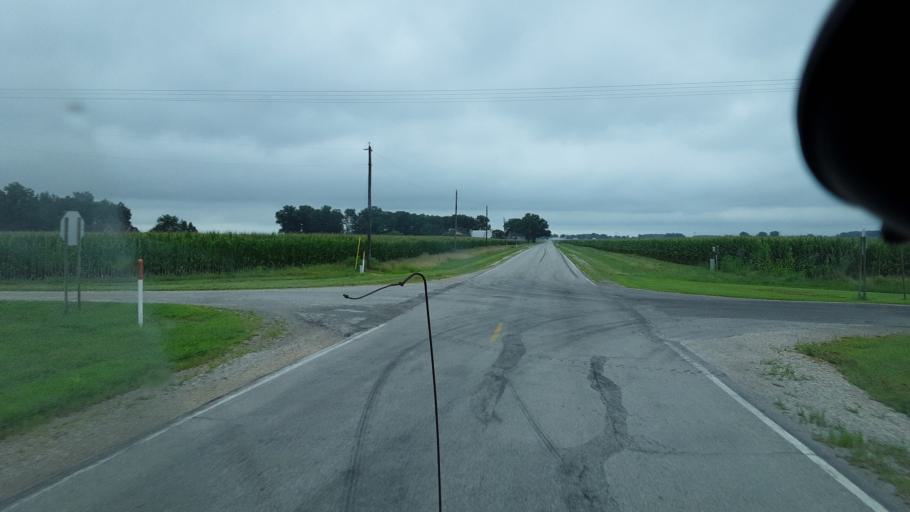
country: US
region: Indiana
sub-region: Wells County
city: Bluffton
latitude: 40.8012
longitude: -85.0907
